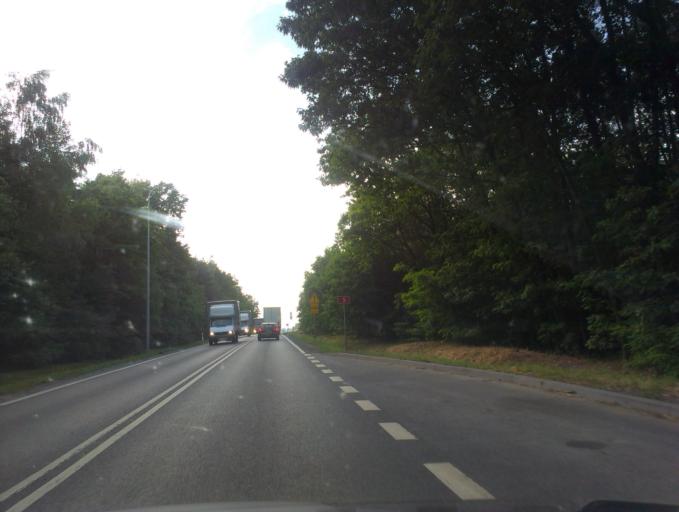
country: PL
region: Lower Silesian Voivodeship
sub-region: Powiat trzebnicki
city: Trzebnica
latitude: 51.3466
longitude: 17.0243
